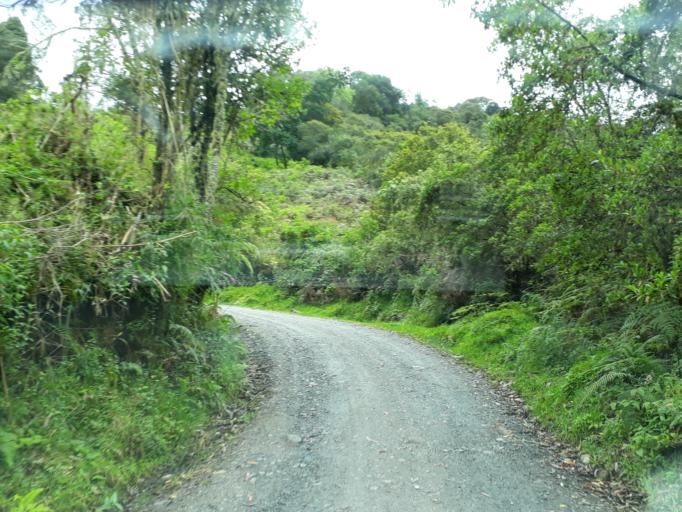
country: CO
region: Cundinamarca
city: Junin
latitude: 4.6838
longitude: -73.6750
